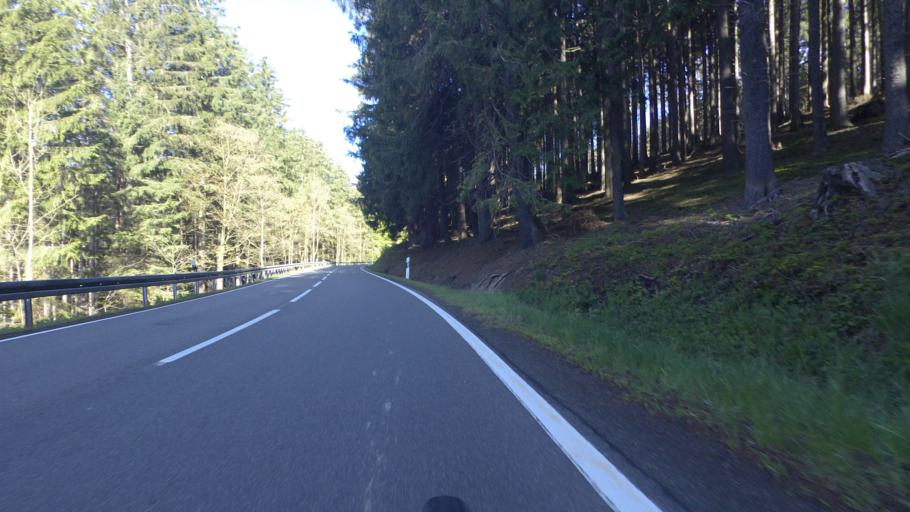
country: DE
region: Saxony-Anhalt
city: Benneckenstein
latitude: 51.7572
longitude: 10.7043
